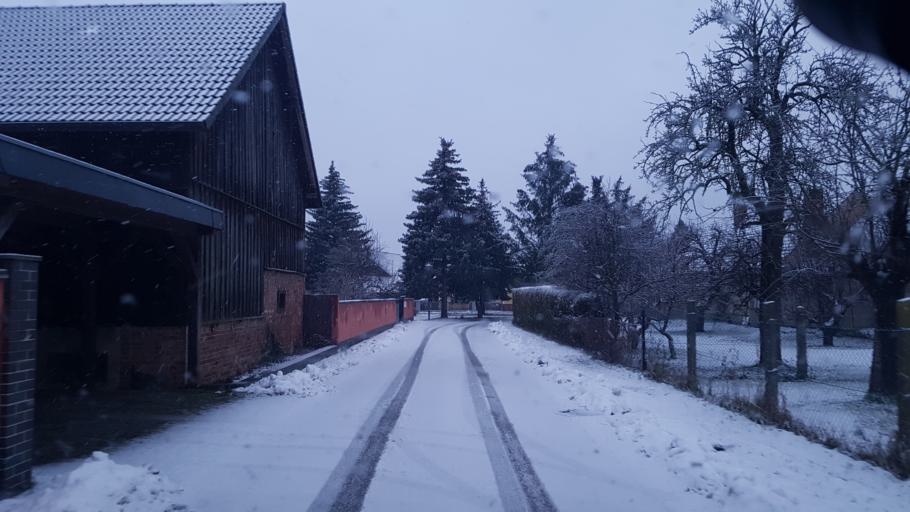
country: DE
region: Brandenburg
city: Janschwalde
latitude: 51.8950
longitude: 14.5138
